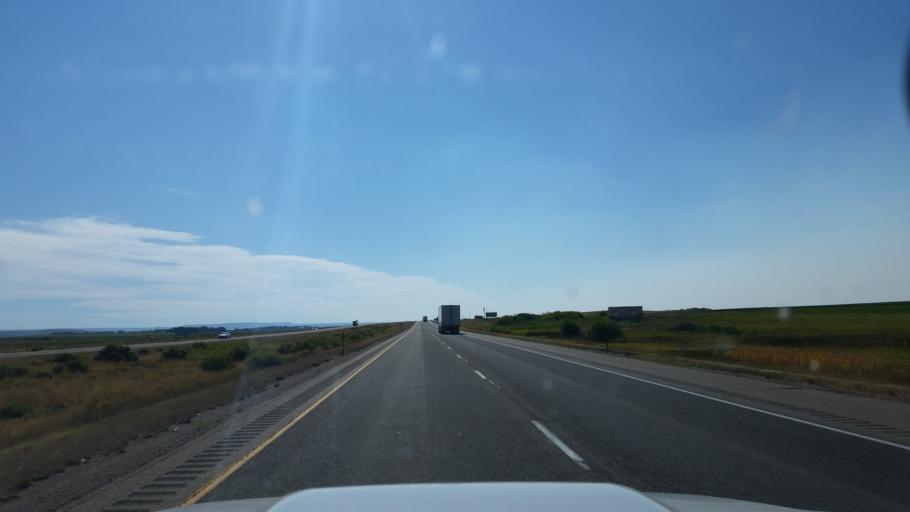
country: US
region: Wyoming
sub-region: Uinta County
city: Lyman
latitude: 41.3739
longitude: -110.2497
